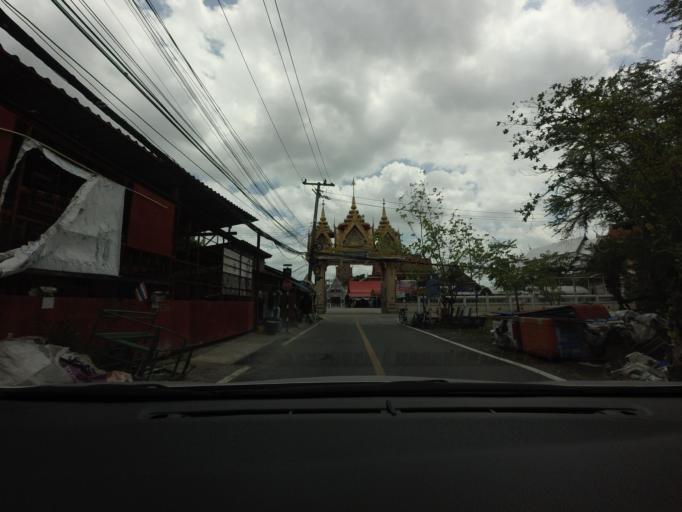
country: TH
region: Samut Prakan
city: Phra Samut Chedi
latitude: 13.6183
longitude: 100.5748
